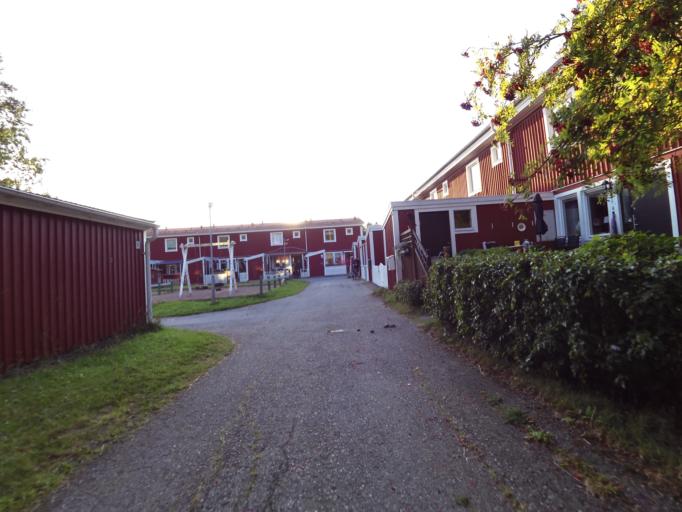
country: SE
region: Gaevleborg
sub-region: Gavle Kommun
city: Gavle
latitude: 60.6653
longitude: 17.2396
